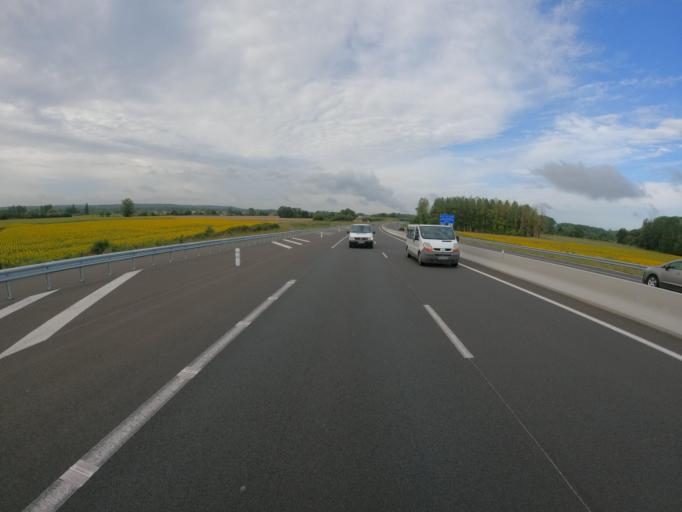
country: FR
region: Centre
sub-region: Departement d'Indre-et-Loire
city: Restigne
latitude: 47.2790
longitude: 0.2762
